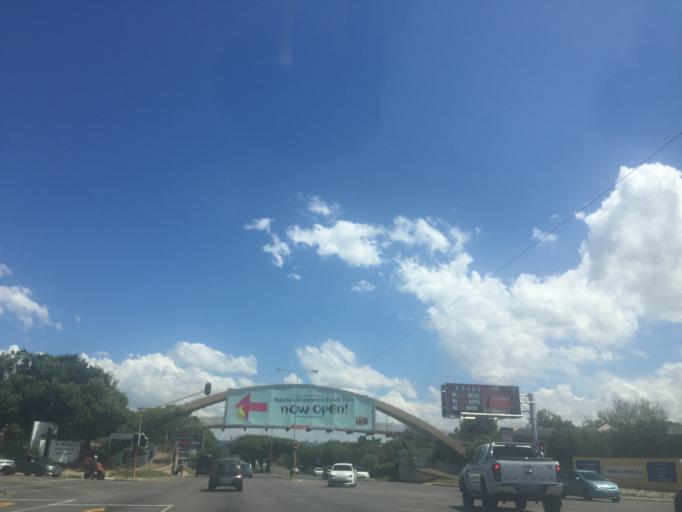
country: ZA
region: Gauteng
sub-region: City of Johannesburg Metropolitan Municipality
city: Midrand
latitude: -26.0602
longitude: 28.0236
